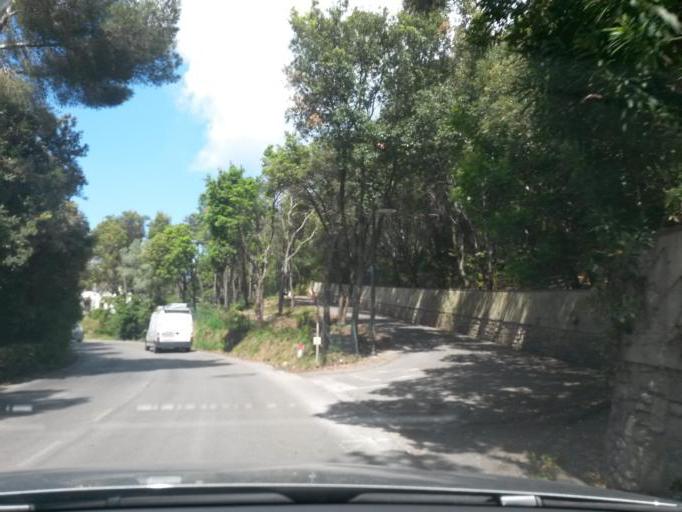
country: IT
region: Tuscany
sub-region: Provincia di Livorno
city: Campo nell'Elba
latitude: 42.7863
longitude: 10.2383
